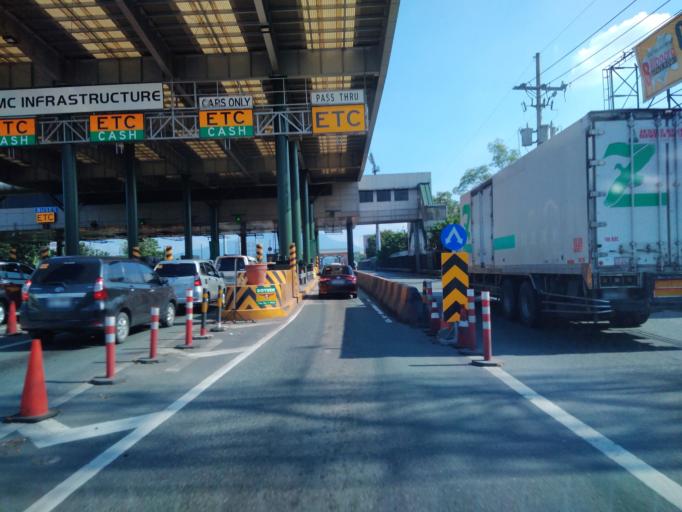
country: PH
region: Calabarzon
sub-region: Province of Laguna
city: Prinza
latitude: 14.2200
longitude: 121.1245
